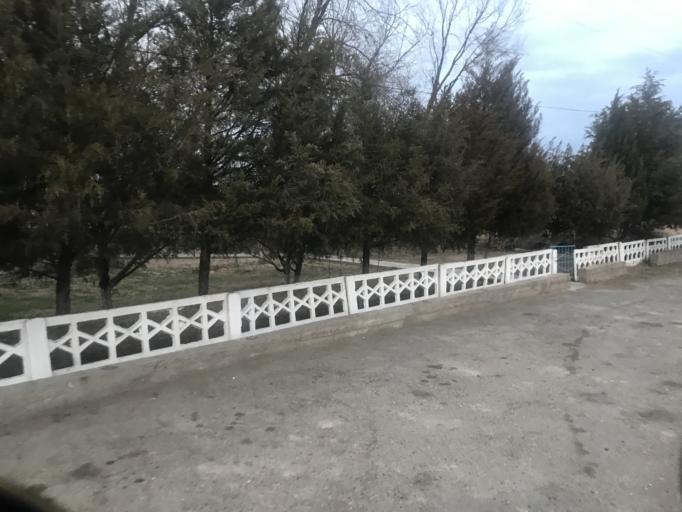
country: KZ
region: Ongtustik Qazaqstan
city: Shardara
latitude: 41.2496
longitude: 67.9022
